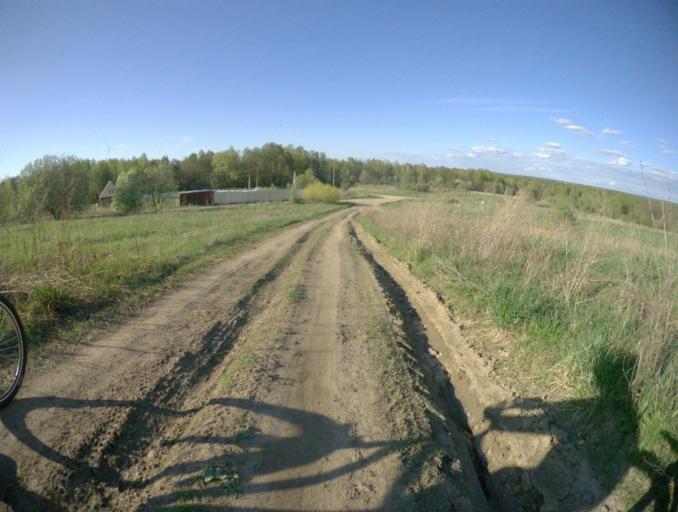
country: RU
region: Vladimir
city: Raduzhnyy
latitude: 56.0001
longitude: 40.3710
